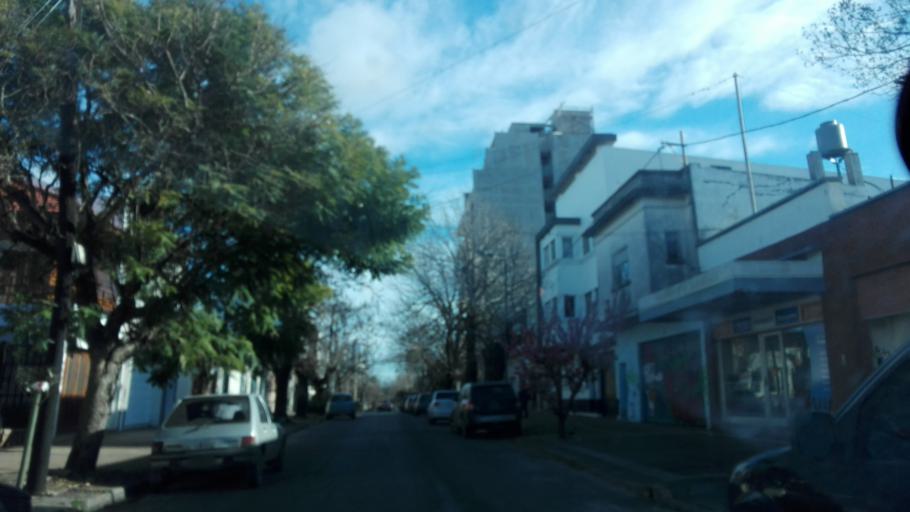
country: AR
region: Buenos Aires
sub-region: Partido de La Plata
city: La Plata
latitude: -34.9329
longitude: -57.9508
